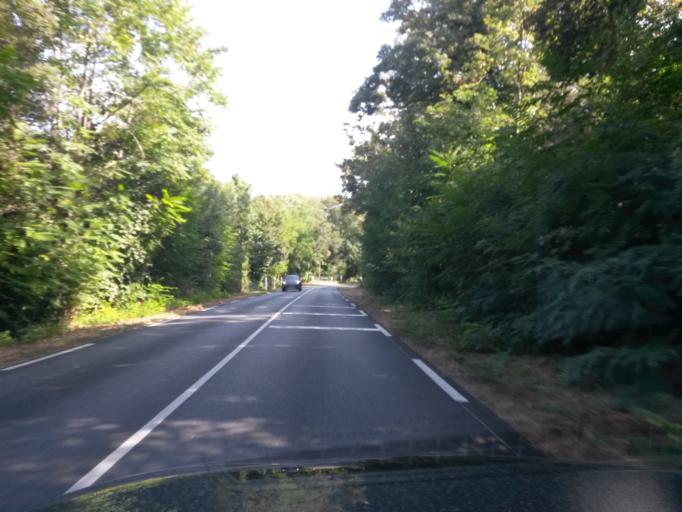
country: FR
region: Pays de la Loire
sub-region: Departement de la Vendee
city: Olonne-sur-Mer
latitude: 46.5596
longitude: -1.8108
